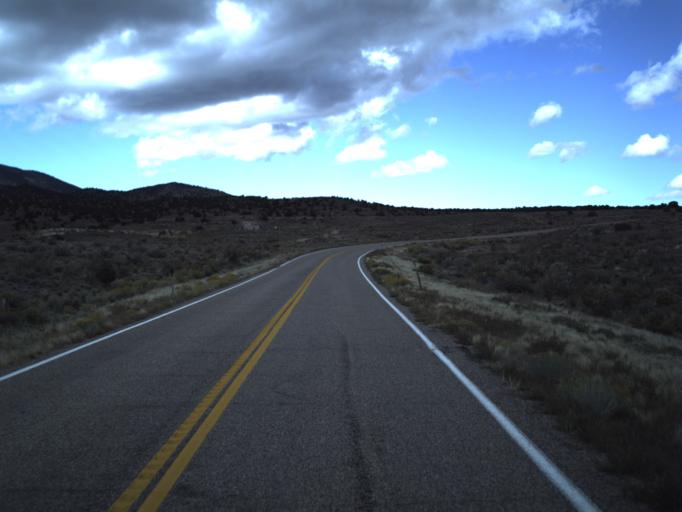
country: US
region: Utah
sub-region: Beaver County
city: Milford
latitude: 38.4540
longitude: -113.2593
